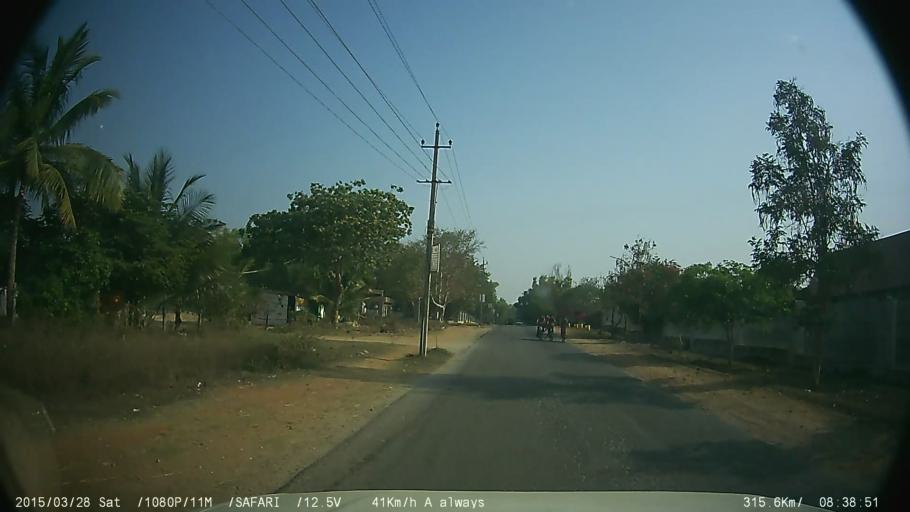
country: IN
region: Karnataka
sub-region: Mysore
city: Mysore
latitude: 12.3591
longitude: 76.5809
